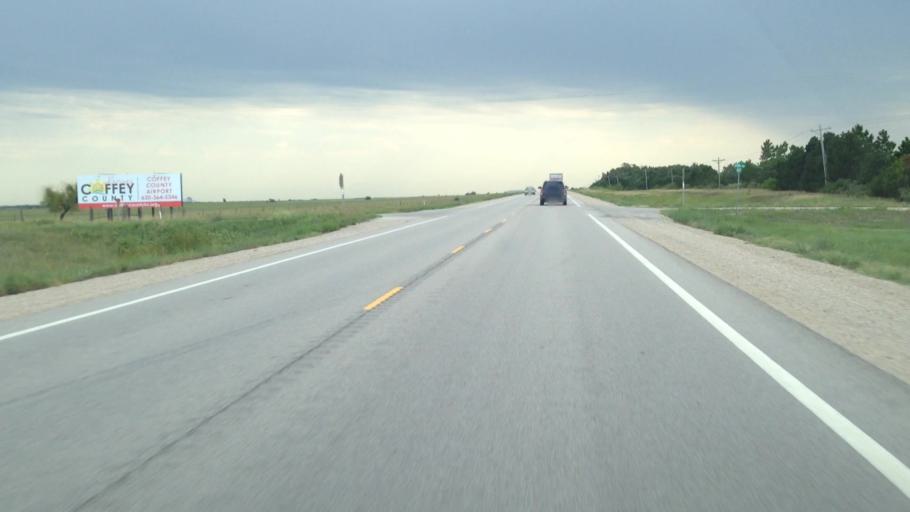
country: US
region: Kansas
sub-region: Coffey County
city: Burlington
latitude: 38.3184
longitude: -95.7290
